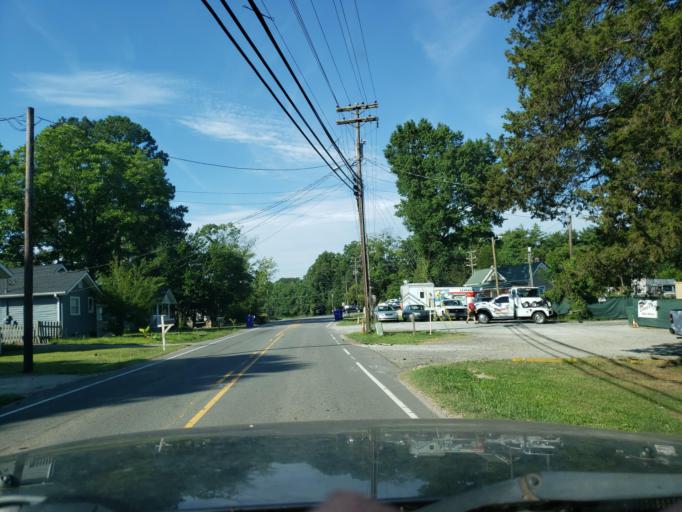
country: US
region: North Carolina
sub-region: Durham County
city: Durham
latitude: 35.9587
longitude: -78.8721
